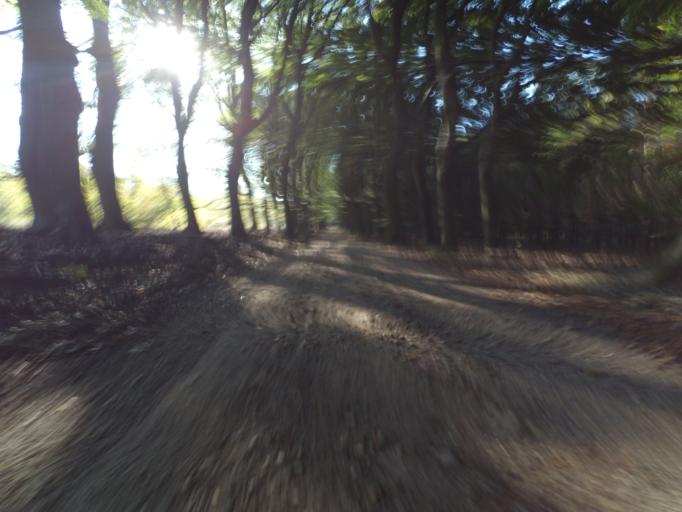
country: NL
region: Gelderland
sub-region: Gemeente Apeldoorn
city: Uddel
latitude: 52.2186
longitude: 5.8135
